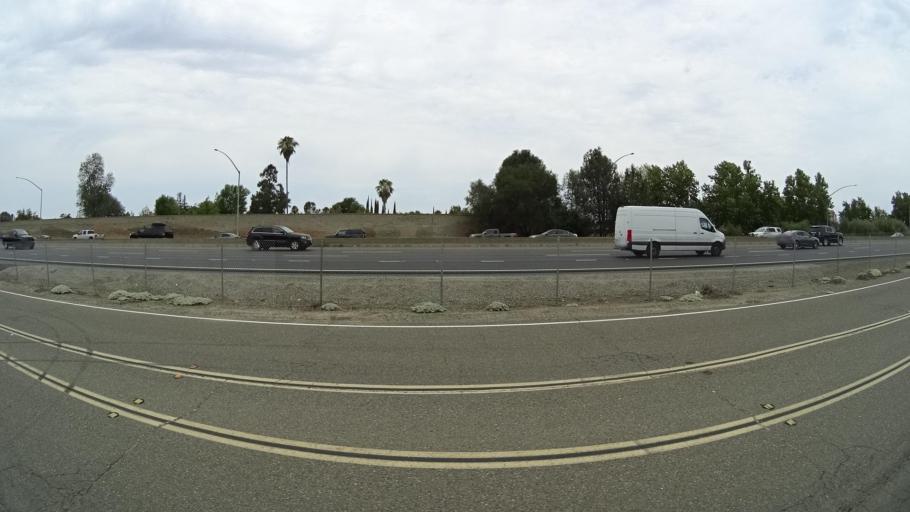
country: US
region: California
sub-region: Placer County
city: Rocklin
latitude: 38.7854
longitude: -121.2255
